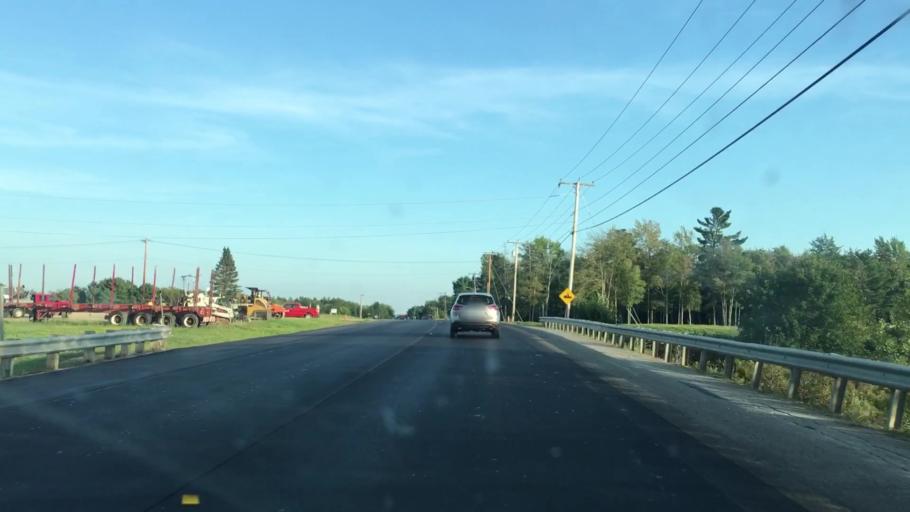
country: US
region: Maine
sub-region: Penobscot County
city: Hampden
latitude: 44.7673
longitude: -68.8550
